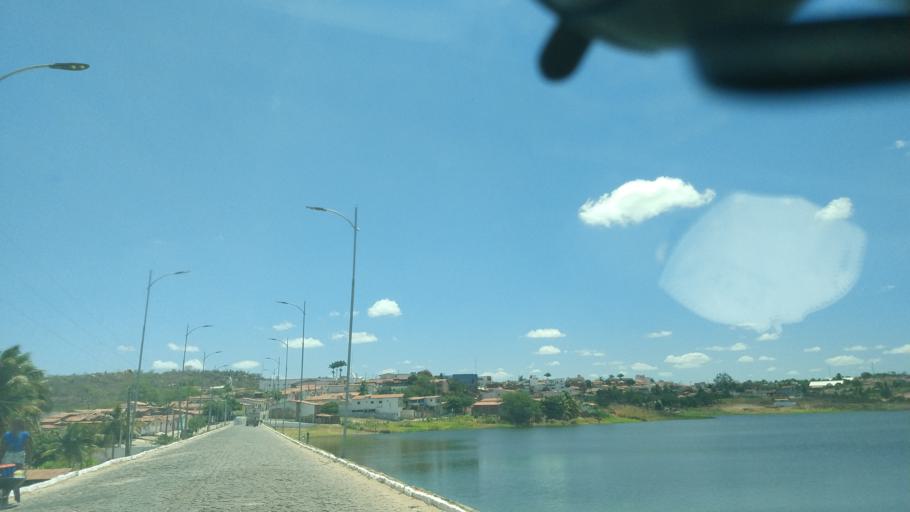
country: BR
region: Rio Grande do Norte
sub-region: Cerro Cora
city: Cerro Cora
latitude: -6.0406
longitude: -36.3466
